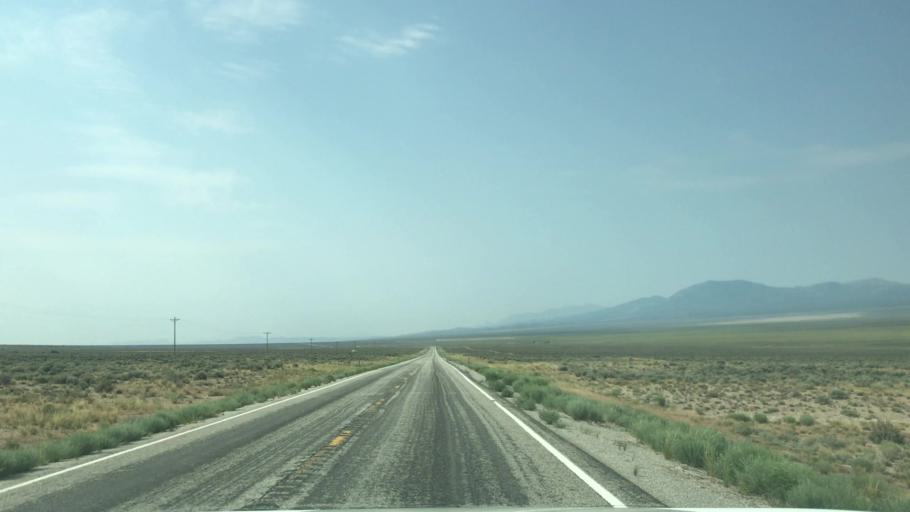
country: US
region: Nevada
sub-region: White Pine County
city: McGill
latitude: 39.0952
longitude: -114.4371
